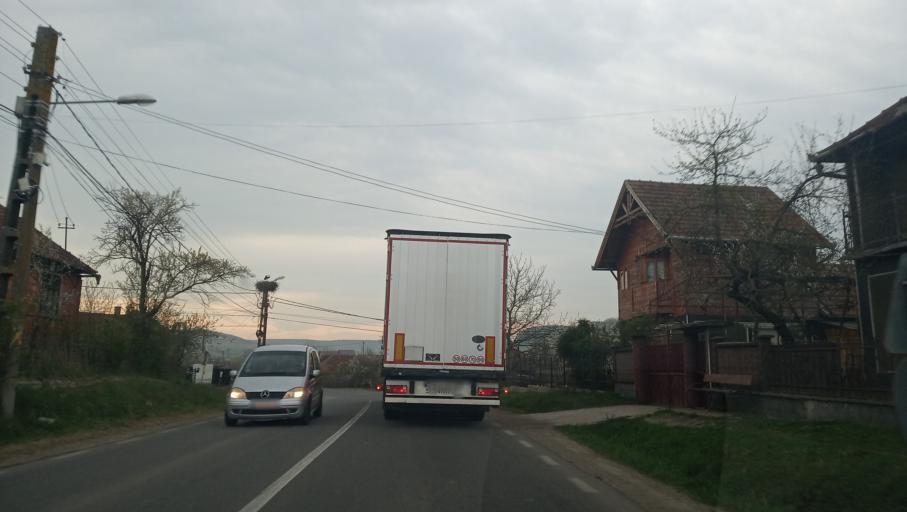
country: RO
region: Bihor
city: Hidiselu de Sus
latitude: 46.9464
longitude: 22.0231
